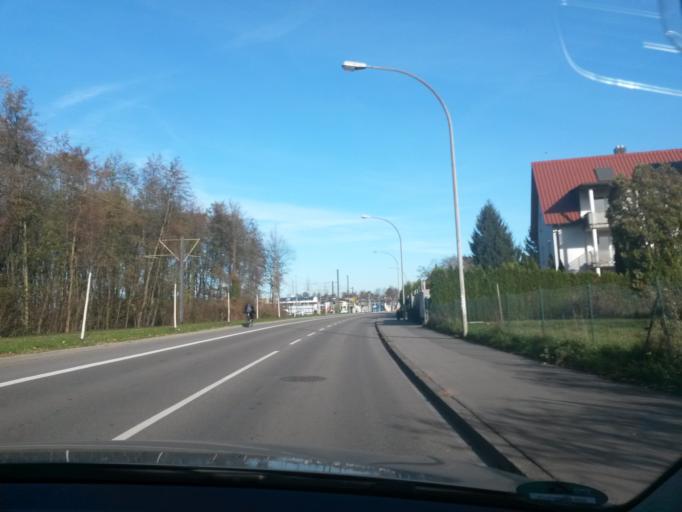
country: DE
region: Baden-Wuerttemberg
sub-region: Freiburg Region
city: Gundelfingen
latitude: 48.0329
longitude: 7.8630
